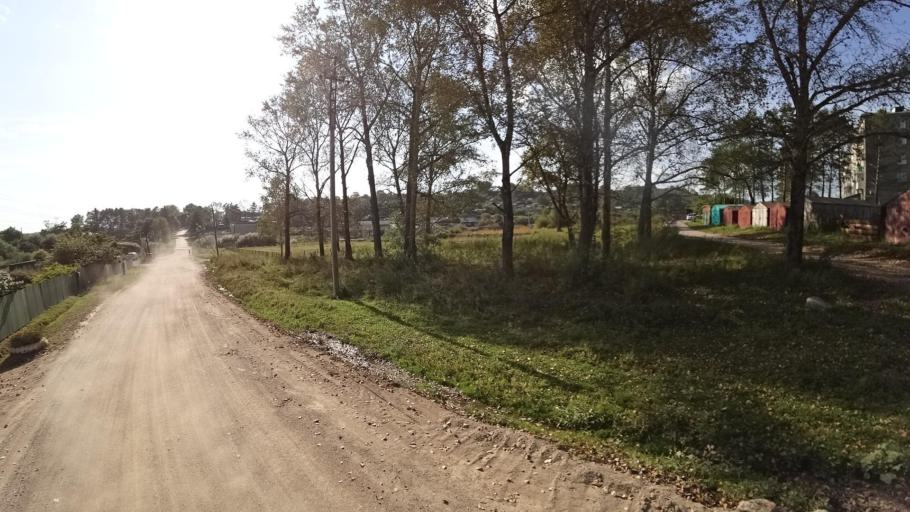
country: RU
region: Jewish Autonomous Oblast
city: Birakan
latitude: 48.9949
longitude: 131.7239
